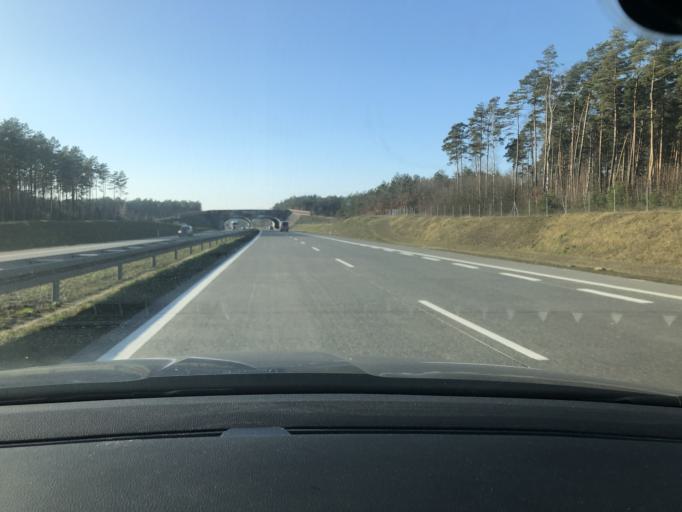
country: PL
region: Lubusz
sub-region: Powiat sulecinski
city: Torzym
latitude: 52.3266
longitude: 15.1541
